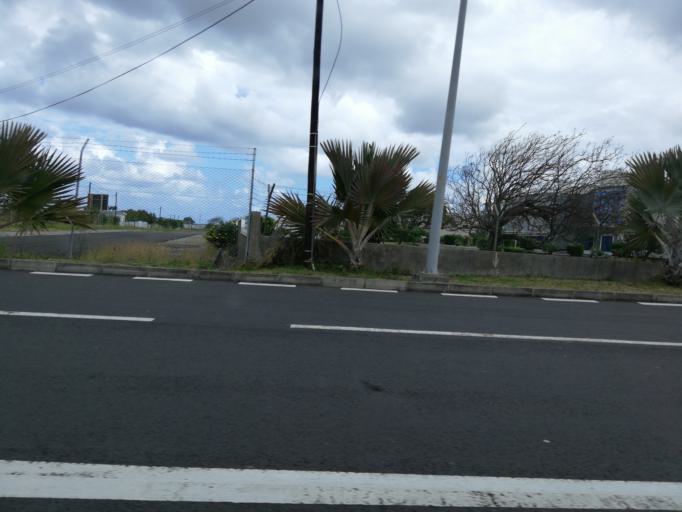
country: MU
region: Grand Port
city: Plaine Magnien
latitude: -20.4354
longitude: 57.6763
